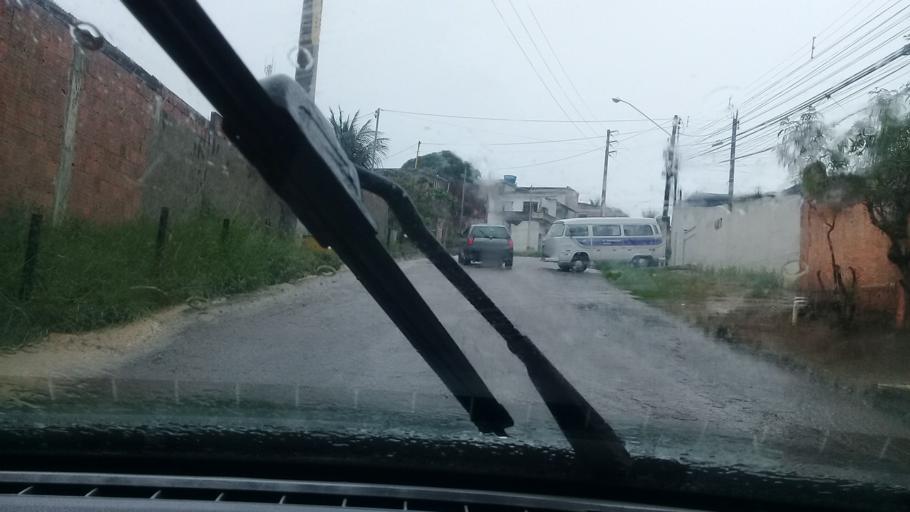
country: BR
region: Pernambuco
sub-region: Paulista
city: Paulista
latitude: -7.9521
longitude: -34.8891
